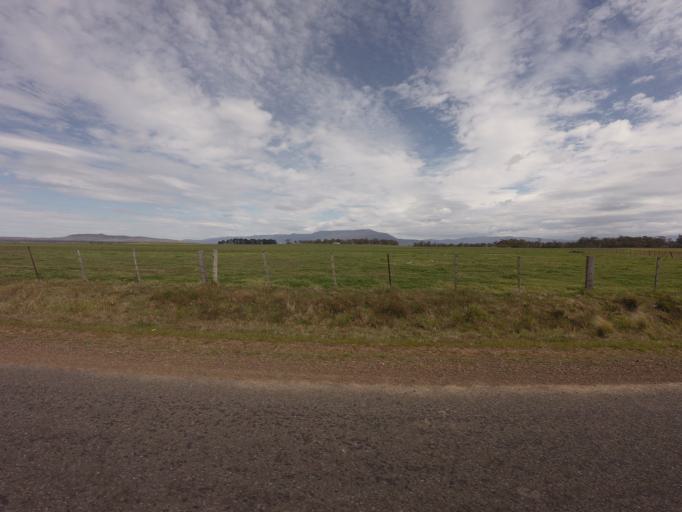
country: AU
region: Tasmania
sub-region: Northern Midlands
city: Evandale
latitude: -41.8000
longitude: 147.2632
